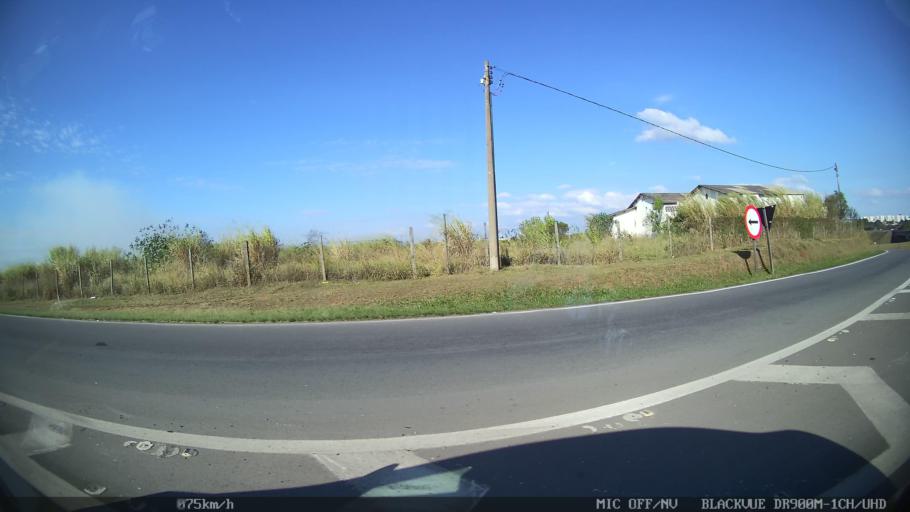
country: BR
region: Sao Paulo
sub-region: Piracicaba
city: Piracicaba
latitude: -22.7196
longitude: -47.6067
